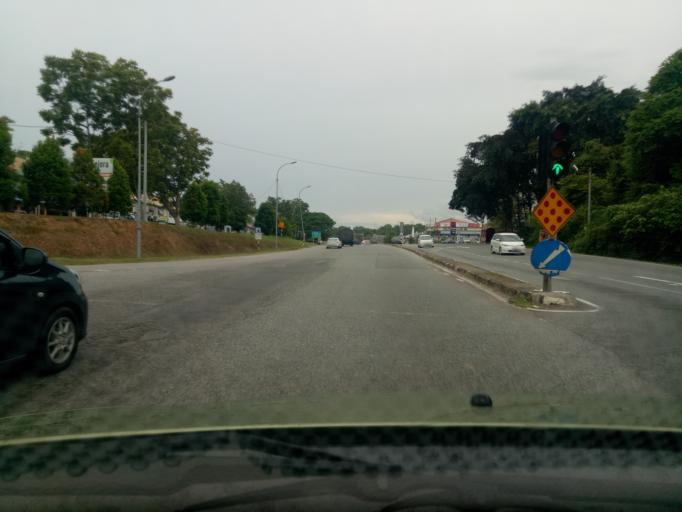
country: MY
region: Kedah
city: Sungai Petani
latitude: 5.6808
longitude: 100.5091
